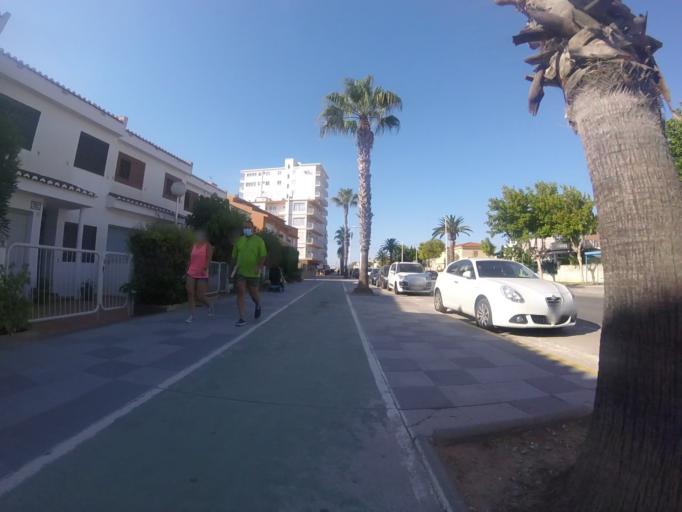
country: ES
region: Valencia
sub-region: Provincia de Castello
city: Benicarlo
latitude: 40.4020
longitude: 0.4182
